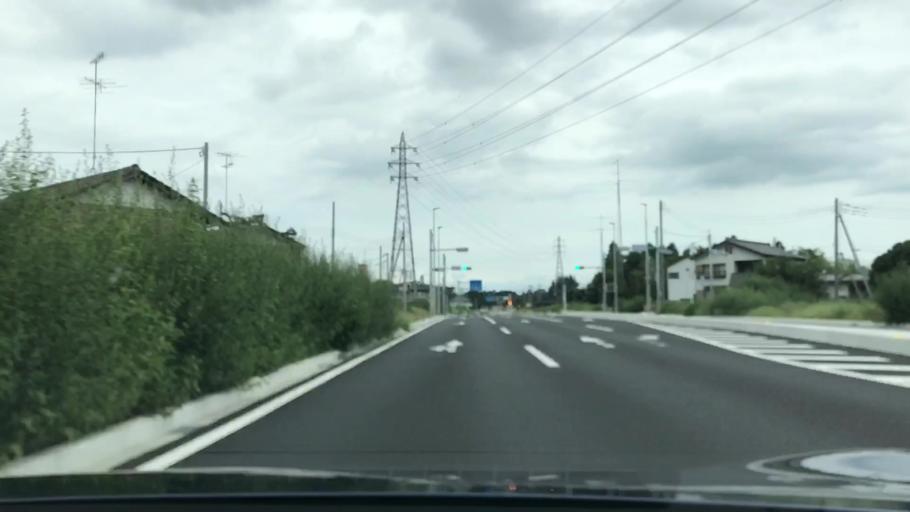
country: JP
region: Gunma
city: Tatebayashi
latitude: 36.2285
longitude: 139.5104
